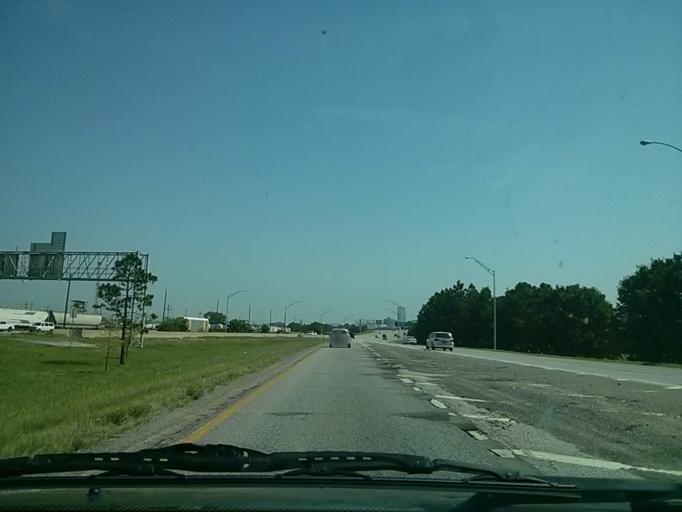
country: US
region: Oklahoma
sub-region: Tulsa County
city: Tulsa
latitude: 36.1135
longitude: -96.0112
